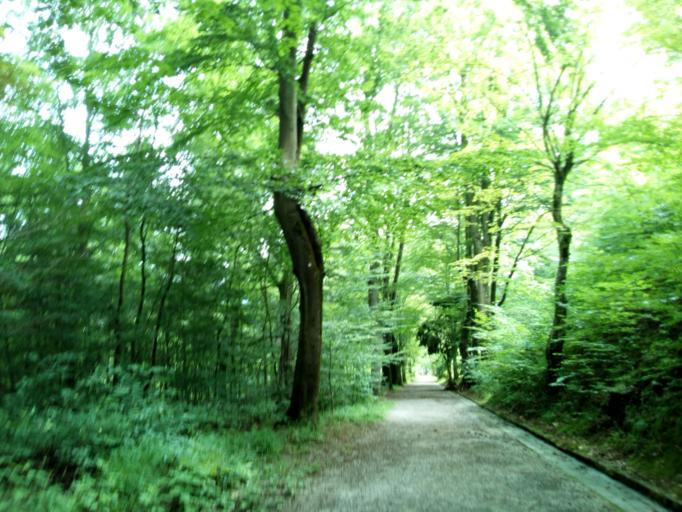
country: DE
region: Hesse
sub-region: Regierungsbezirk Darmstadt
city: Schlangenbad
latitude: 50.0933
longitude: 8.0941
